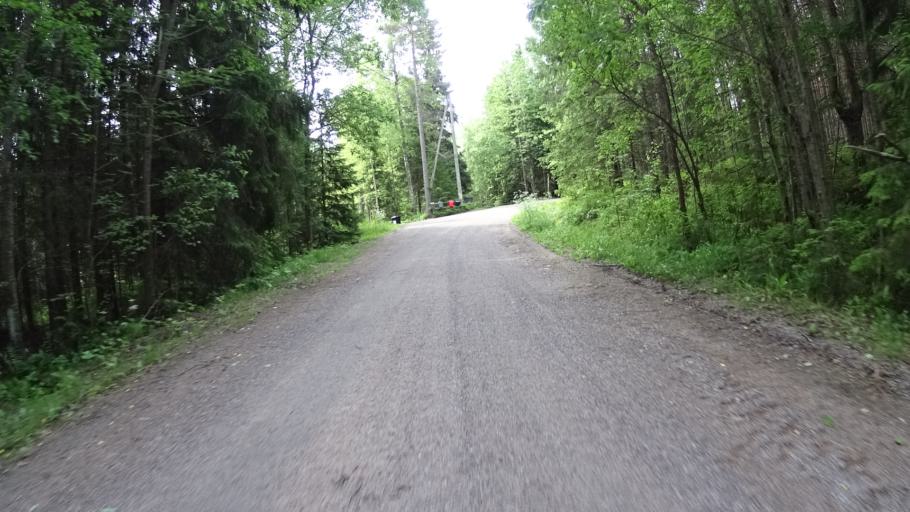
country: FI
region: Uusimaa
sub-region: Helsinki
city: Espoo
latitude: 60.2848
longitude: 24.5145
